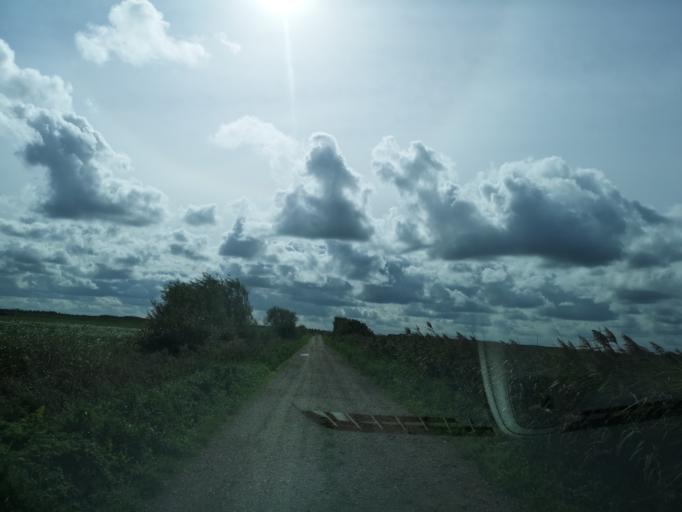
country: DK
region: Central Jutland
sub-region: Ringkobing-Skjern Kommune
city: Tarm
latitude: 55.9335
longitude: 8.5371
